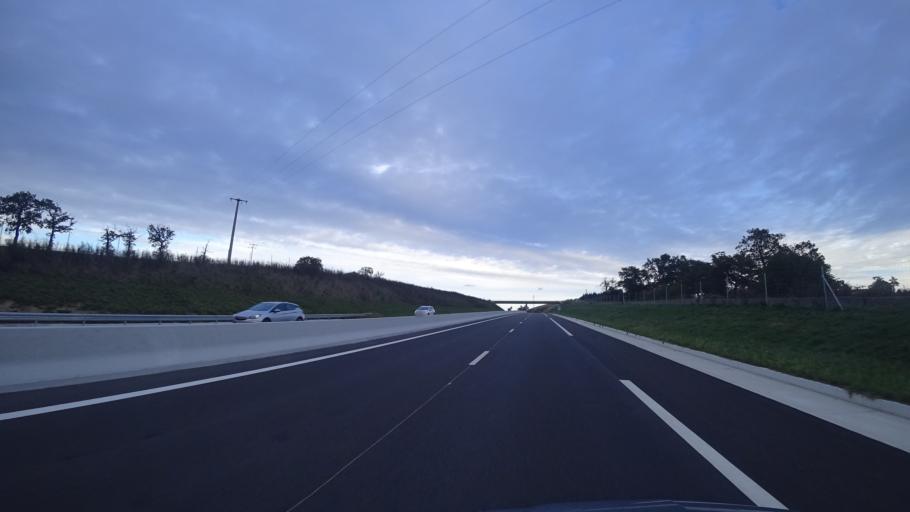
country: FR
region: Midi-Pyrenees
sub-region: Departement de l'Aveyron
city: Baraqueville
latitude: 44.2889
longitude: 2.4659
